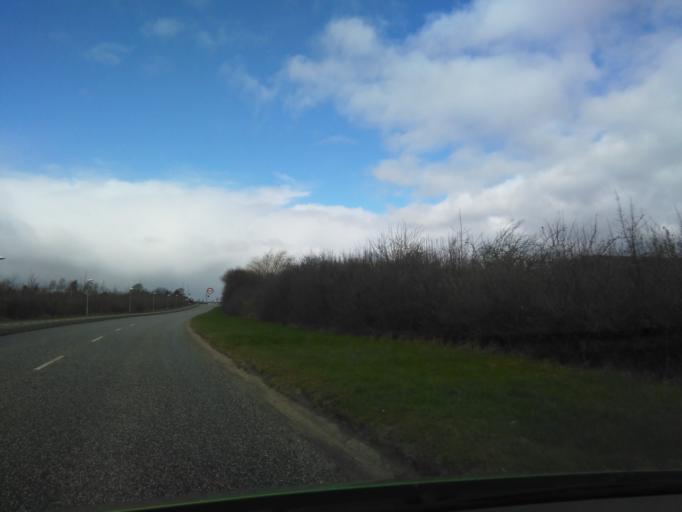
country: DK
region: Central Jutland
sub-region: Arhus Kommune
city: Tranbjerg
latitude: 56.0831
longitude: 10.1270
